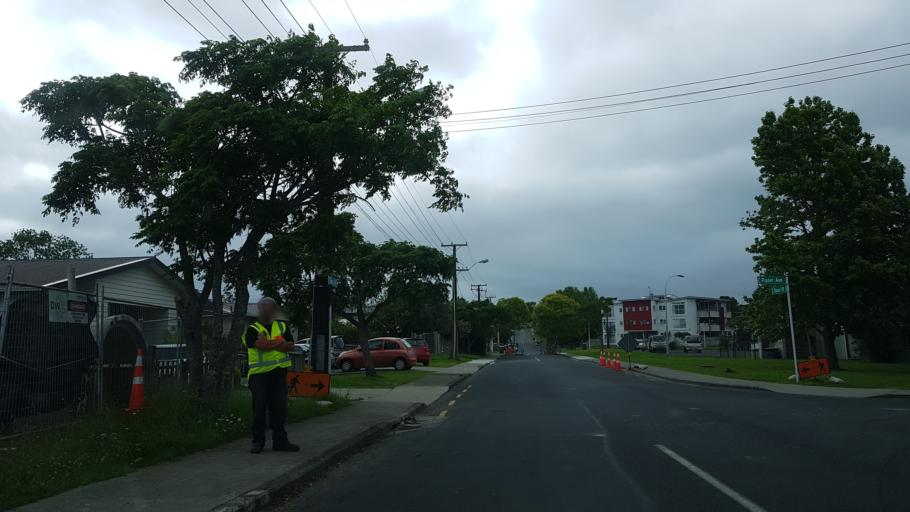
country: NZ
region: Auckland
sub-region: Auckland
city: North Shore
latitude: -36.7961
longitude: 174.7483
